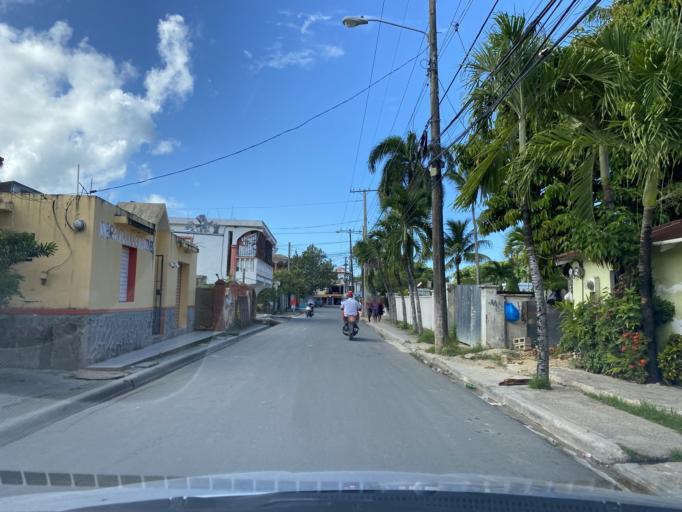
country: DO
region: Samana
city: Las Terrenas
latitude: 19.3114
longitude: -69.5453
